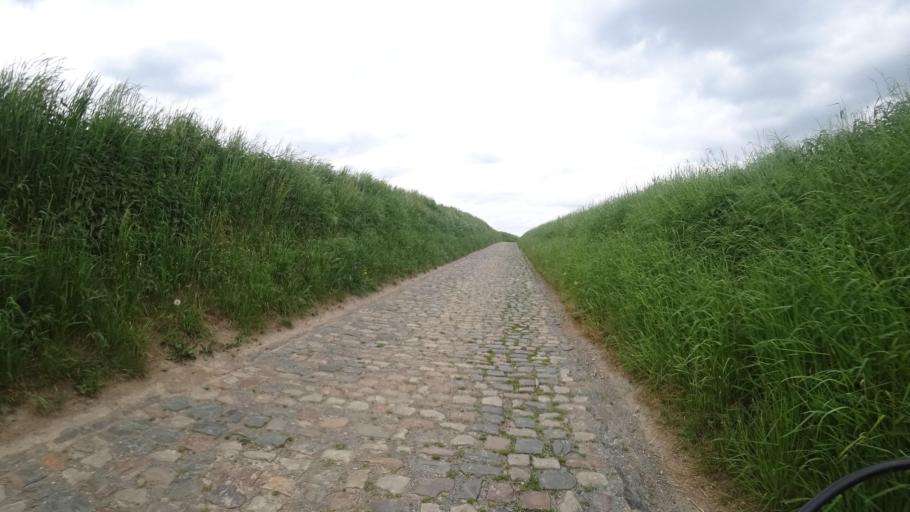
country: BE
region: Wallonia
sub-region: Province du Brabant Wallon
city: Grez-Doiceau
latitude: 50.7251
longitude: 4.6927
